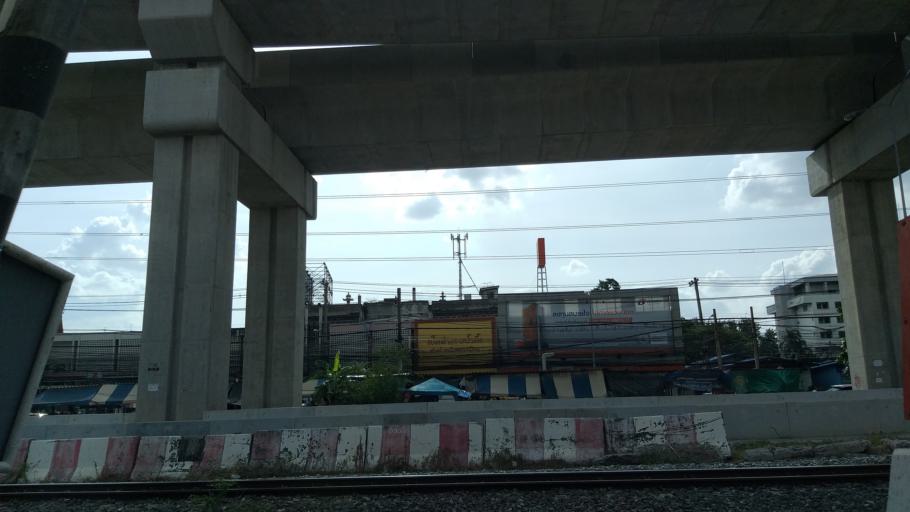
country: TH
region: Bangkok
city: Don Mueang
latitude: 13.9230
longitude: 100.6029
